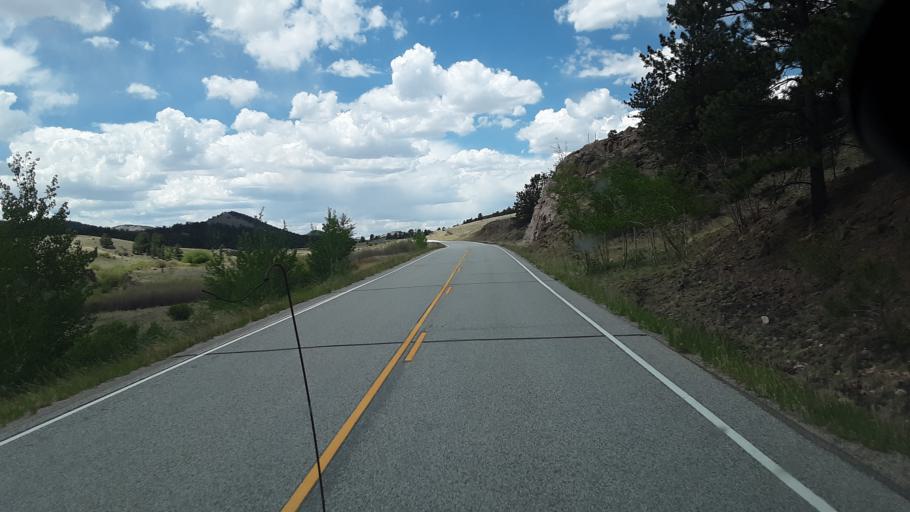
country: US
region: Colorado
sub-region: Teller County
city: Cripple Creek
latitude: 38.7875
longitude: -105.5848
